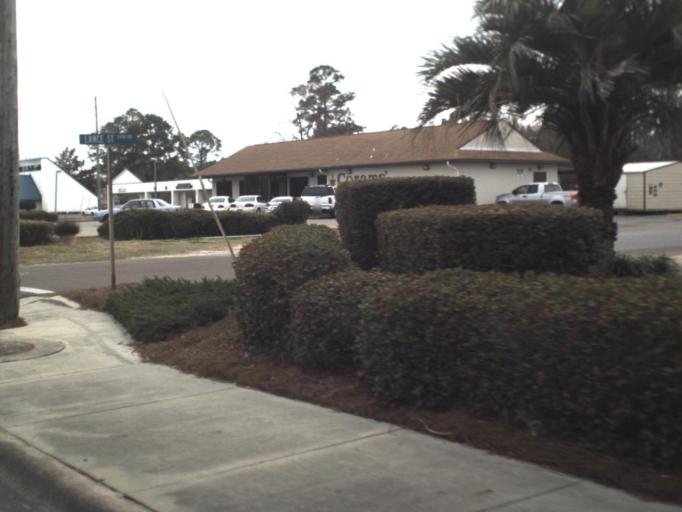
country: US
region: Florida
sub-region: Bay County
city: Parker
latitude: 30.1331
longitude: -85.5913
